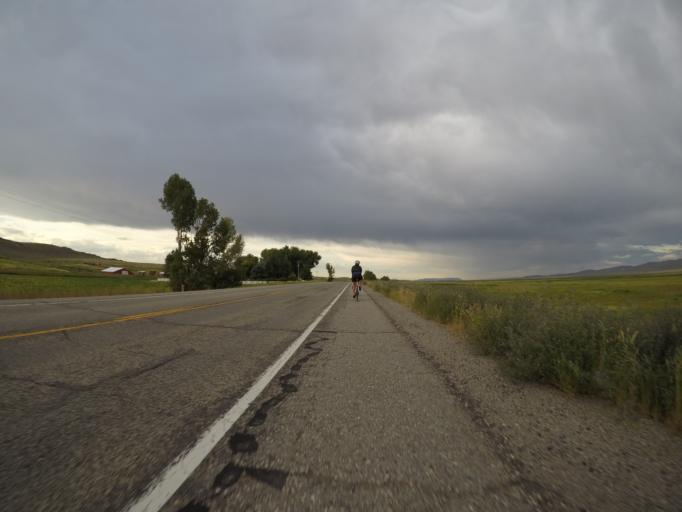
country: US
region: Utah
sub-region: Rich County
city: Randolph
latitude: 42.0265
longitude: -110.9326
